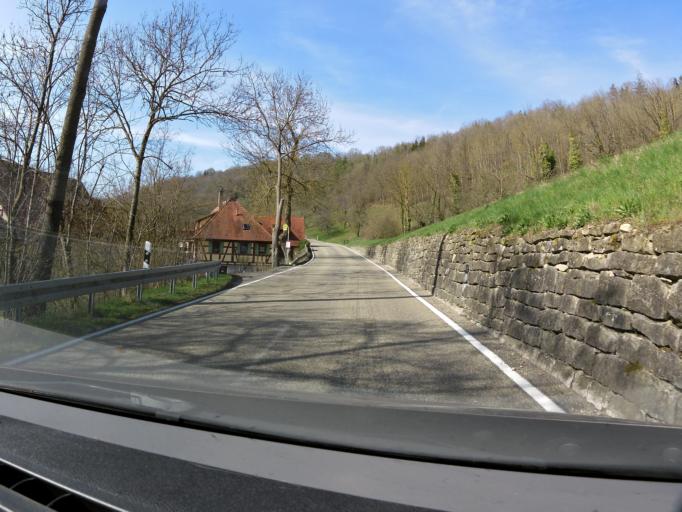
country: DE
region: Bavaria
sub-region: Regierungsbezirk Mittelfranken
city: Rothenburg ob der Tauber
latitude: 49.3963
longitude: 10.1675
